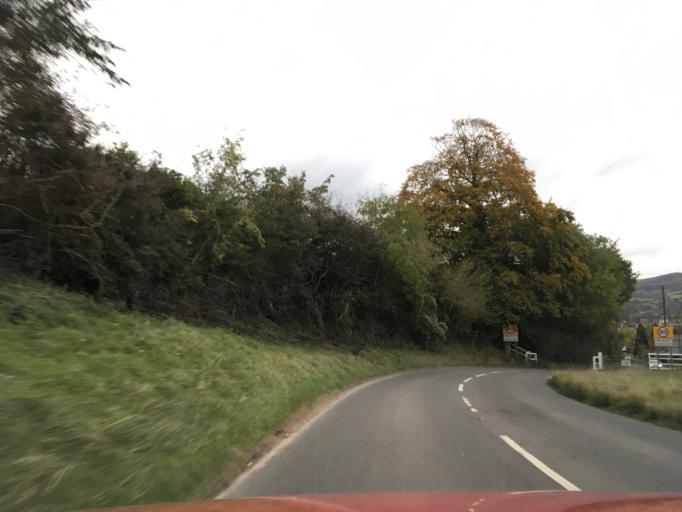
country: GB
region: England
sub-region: Gloucestershire
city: Nailsworth
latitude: 51.7311
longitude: -2.2428
